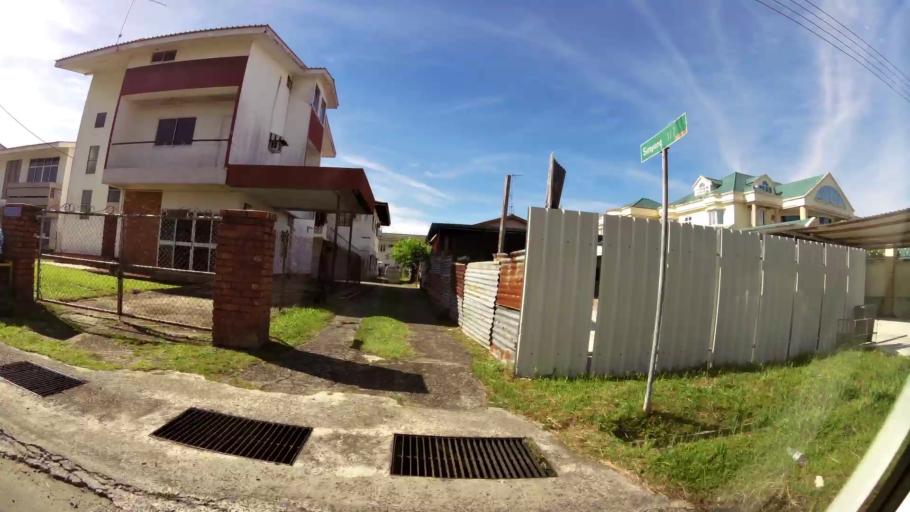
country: BN
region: Belait
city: Kuala Belait
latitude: 4.5856
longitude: 114.2140
